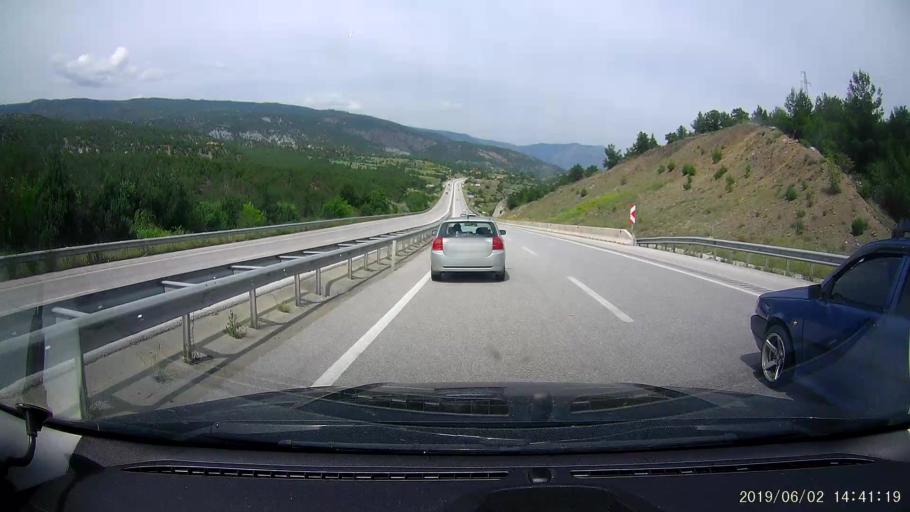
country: TR
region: Corum
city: Hacihamza
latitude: 41.0849
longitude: 34.3378
